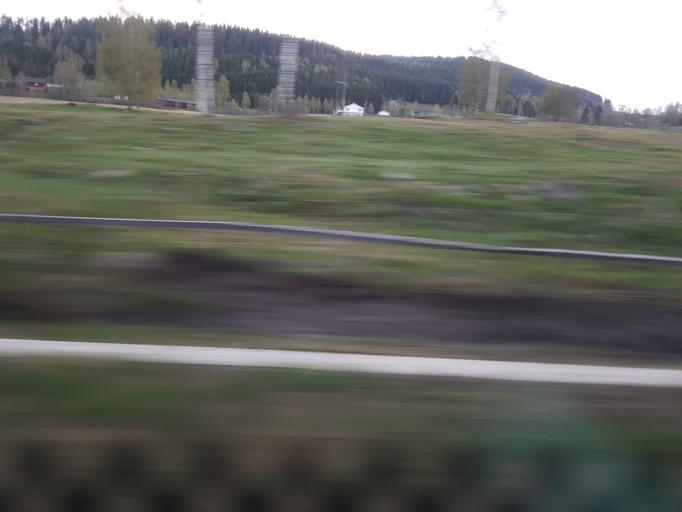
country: NO
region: Hedmark
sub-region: Ringsaker
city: Moelv
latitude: 60.9156
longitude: 10.7658
